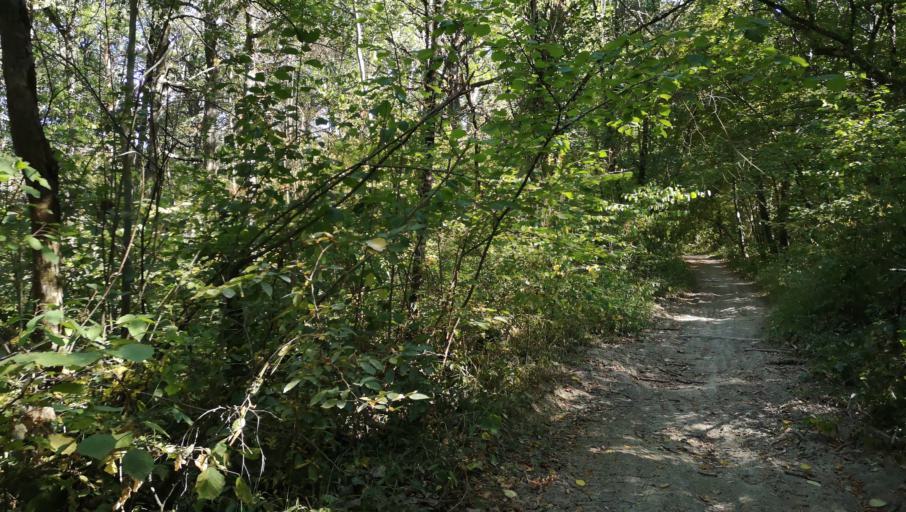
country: FR
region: Centre
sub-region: Departement du Loiret
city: Saran
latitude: 47.9665
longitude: 1.8899
